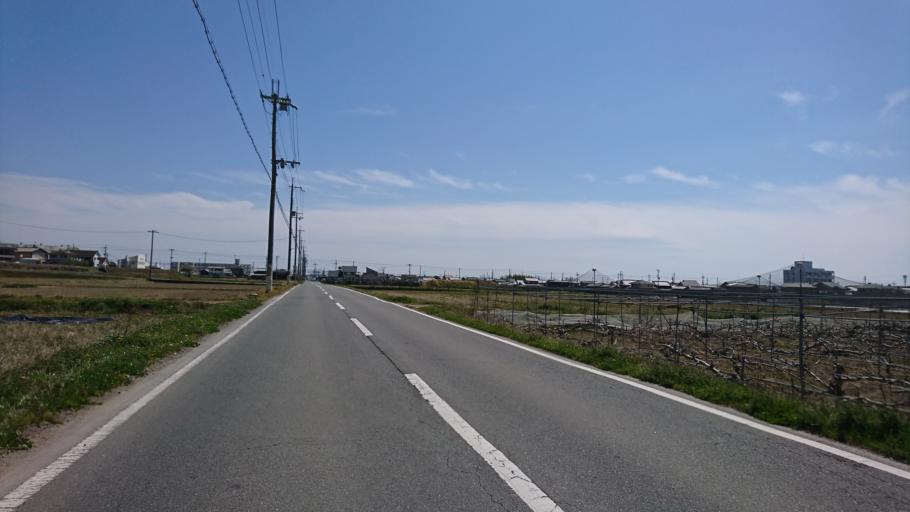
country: JP
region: Hyogo
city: Kakogawacho-honmachi
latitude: 34.7470
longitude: 134.8891
